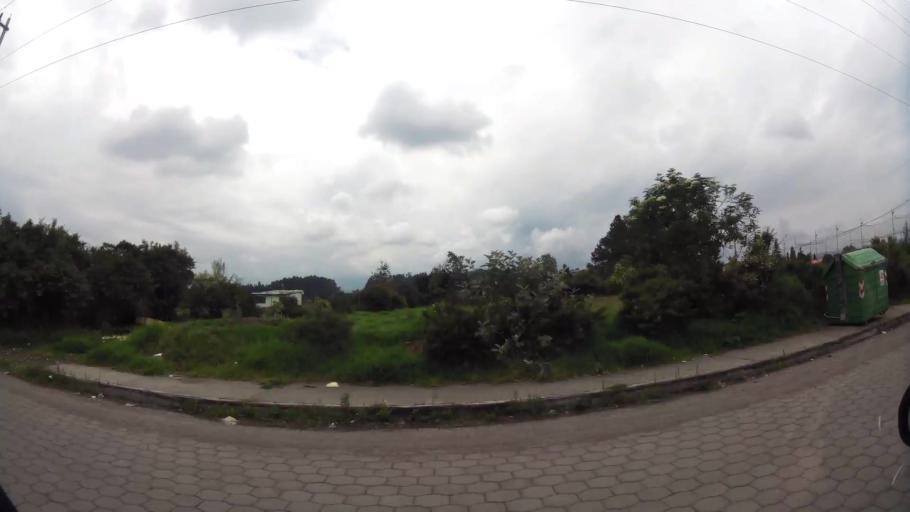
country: EC
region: Pichincha
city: Sangolqui
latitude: -0.3395
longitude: -78.4655
